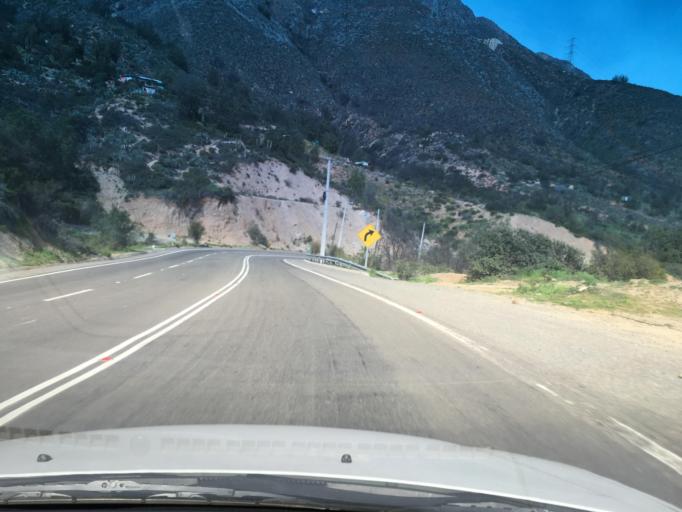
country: CL
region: Valparaiso
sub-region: Provincia de San Felipe
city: Llaillay
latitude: -33.0627
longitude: -71.0246
